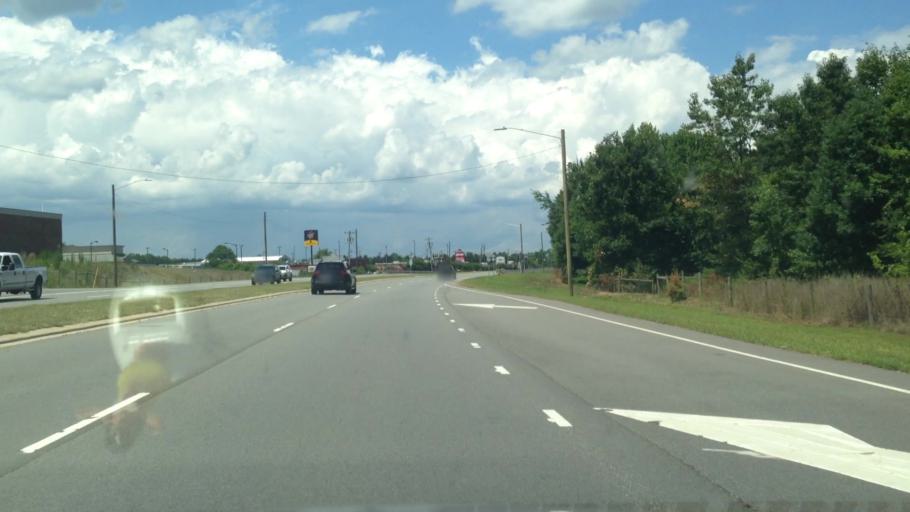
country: US
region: North Carolina
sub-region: Rockingham County
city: Reidsville
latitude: 36.3349
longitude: -79.6929
